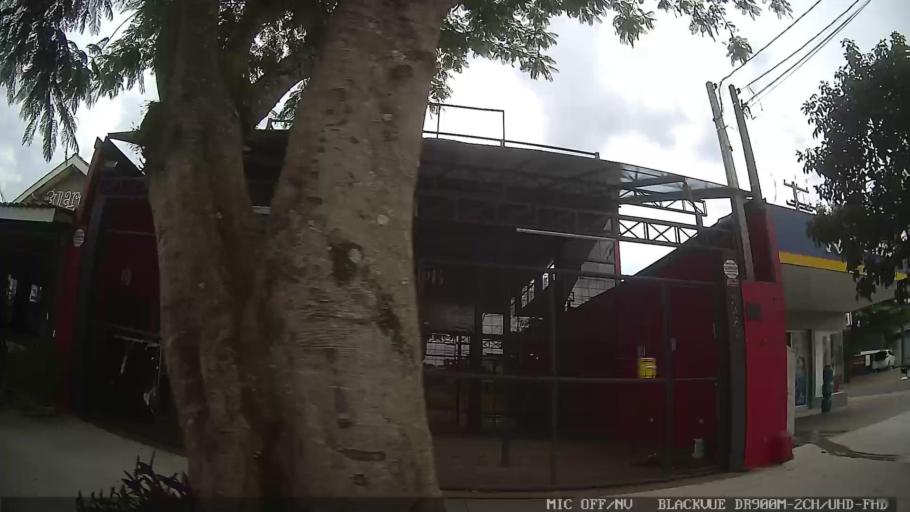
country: BR
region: Sao Paulo
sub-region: Atibaia
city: Atibaia
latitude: -23.1301
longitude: -46.5541
